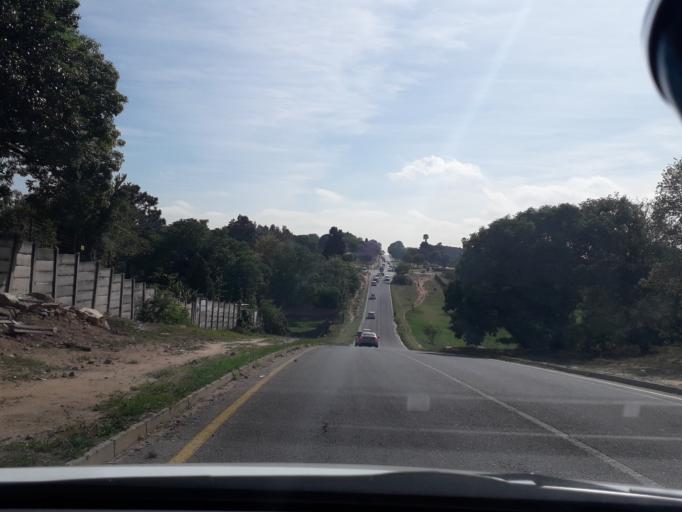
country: ZA
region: Gauteng
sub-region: City of Johannesburg Metropolitan Municipality
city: Roodepoort
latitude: -26.1153
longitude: 27.9436
